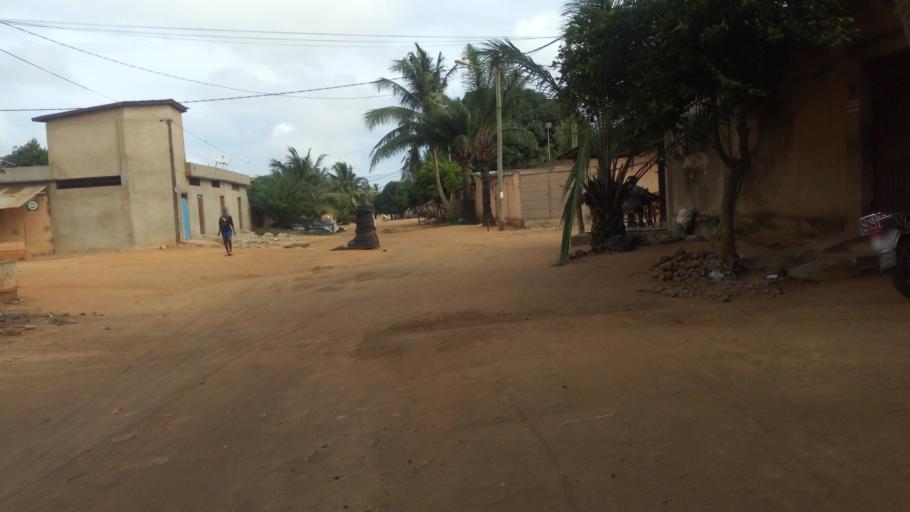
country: TG
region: Maritime
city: Lome
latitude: 6.1896
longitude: 1.1784
